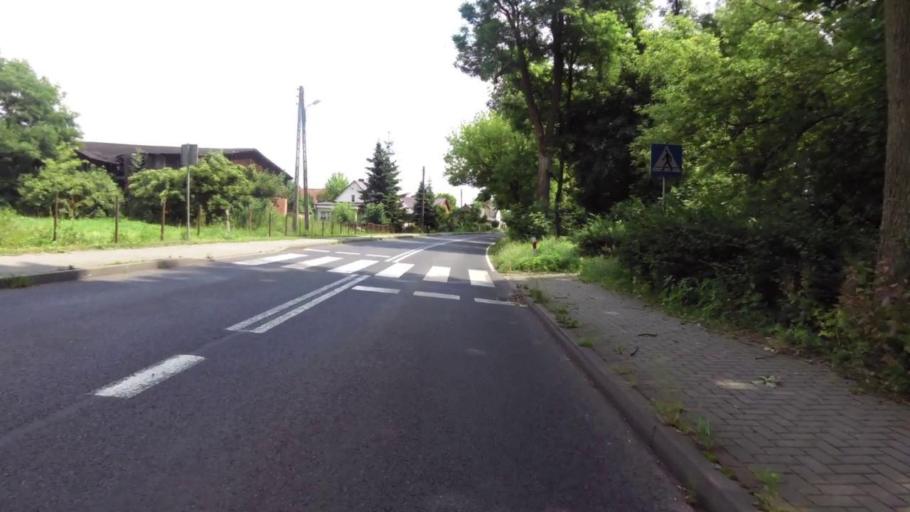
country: PL
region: West Pomeranian Voivodeship
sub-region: Powiat pyrzycki
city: Lipiany
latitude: 52.9994
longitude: 15.0292
